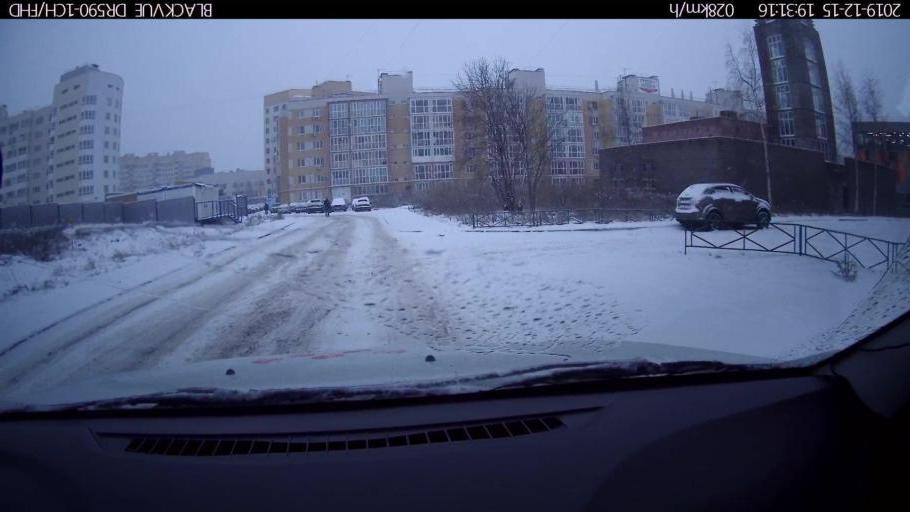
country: RU
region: Nizjnij Novgorod
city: Afonino
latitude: 56.3047
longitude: 44.0746
